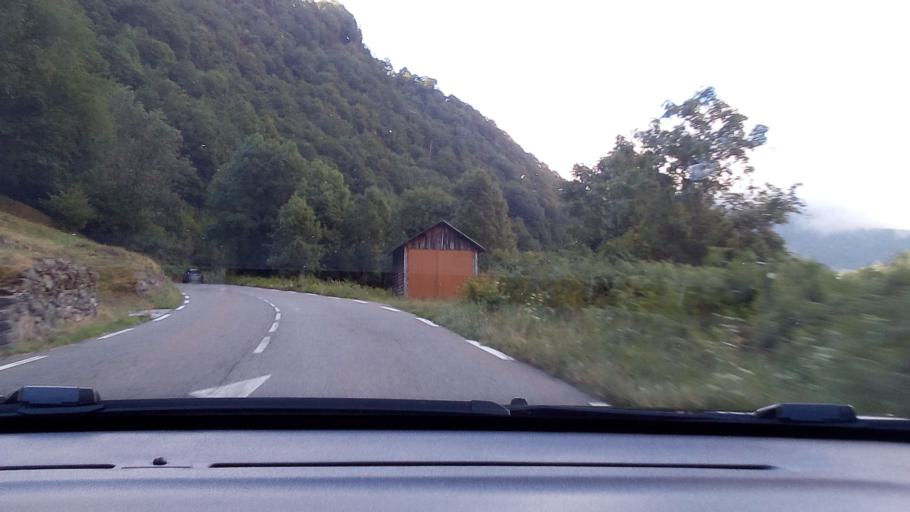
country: ES
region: Aragon
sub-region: Provincia de Huesca
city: Canfranc
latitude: 42.8686
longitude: -0.5514
